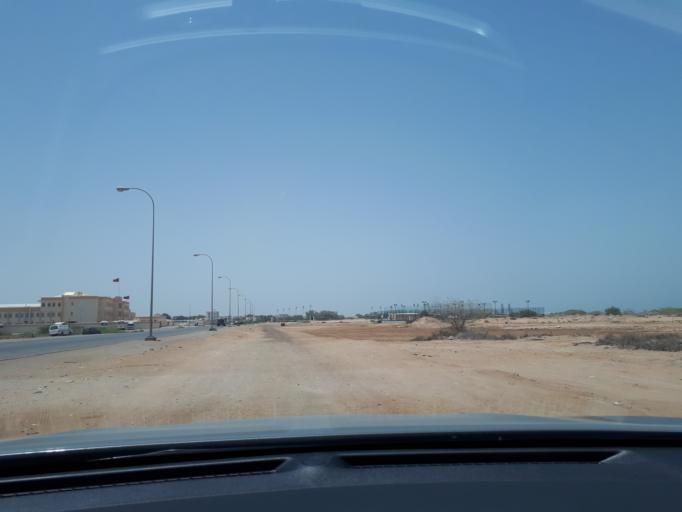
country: OM
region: Muhafazat Masqat
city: As Sib al Jadidah
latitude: 23.6295
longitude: 58.2542
